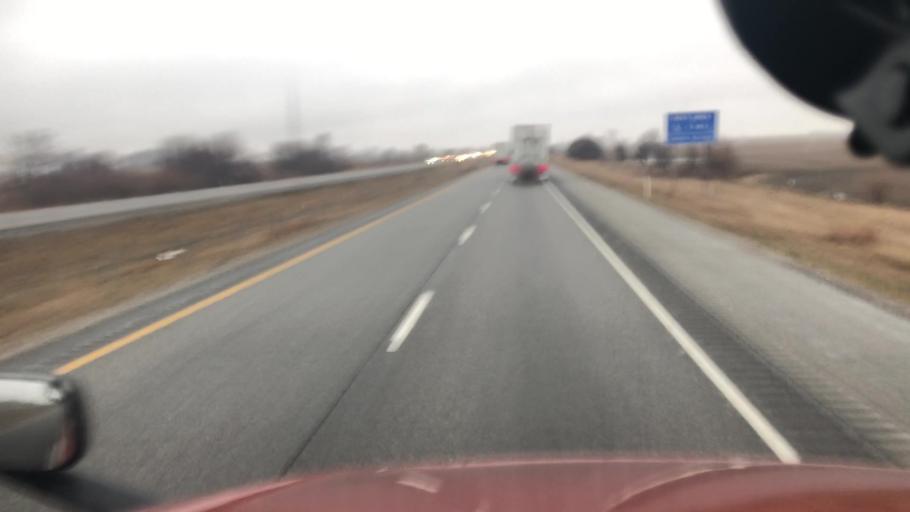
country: US
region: Indiana
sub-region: White County
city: Wolcott
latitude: 40.6810
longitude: -87.0543
